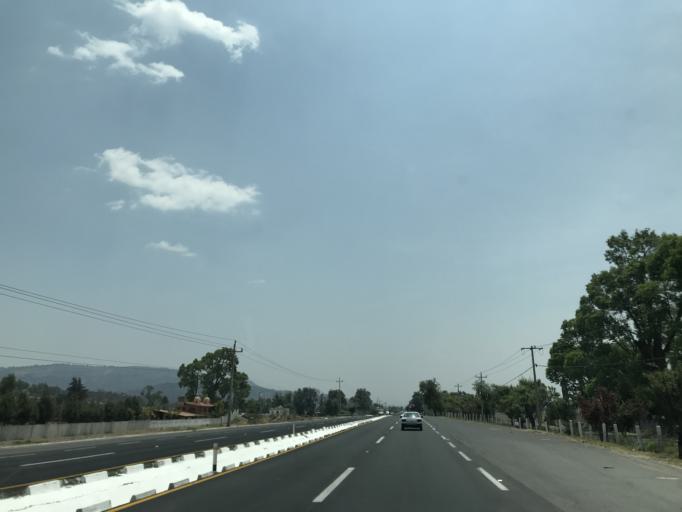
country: MX
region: Tlaxcala
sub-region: Ixtacuixtla de Mariano Matamoros
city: Santa Justina Ecatepec
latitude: 19.3271
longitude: -98.3320
